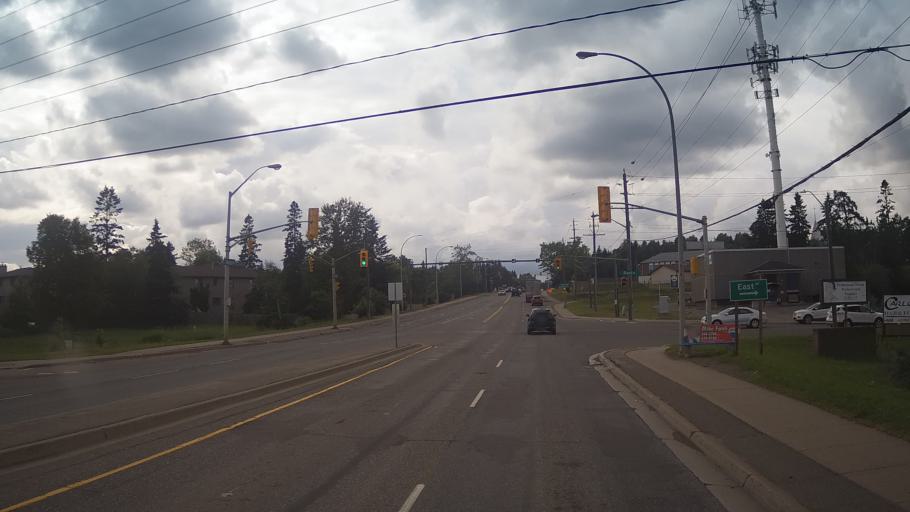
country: CA
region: Ontario
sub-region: Thunder Bay District
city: Thunder Bay
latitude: 48.4525
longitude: -89.2562
